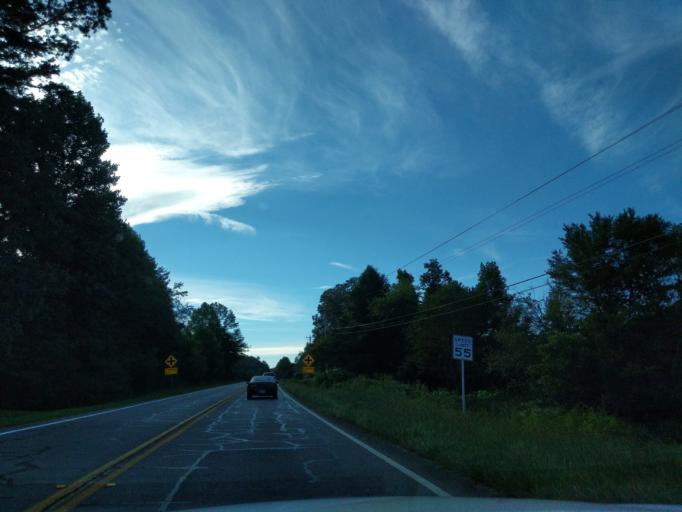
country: US
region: Georgia
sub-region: Fannin County
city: Blue Ridge
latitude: 34.8928
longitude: -84.3518
